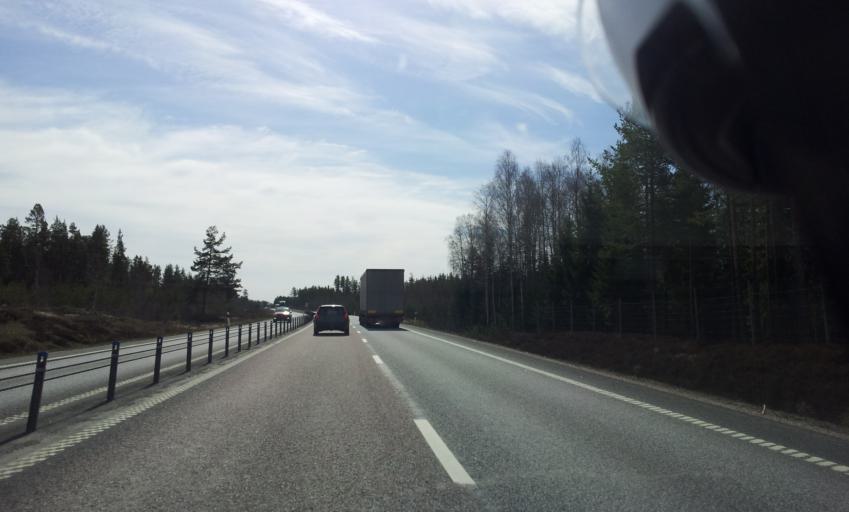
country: SE
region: Gaevleborg
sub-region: Gavle Kommun
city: Norrsundet
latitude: 61.0435
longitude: 16.9627
